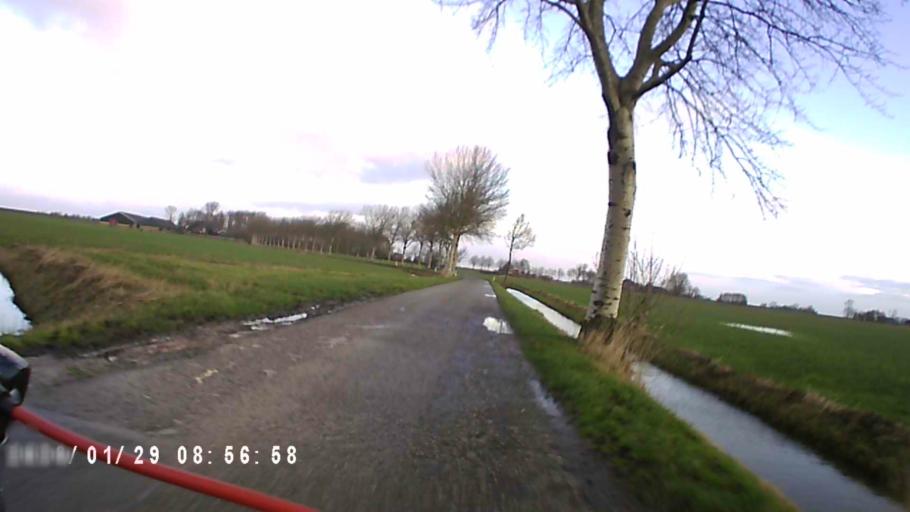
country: NL
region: Groningen
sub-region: Gemeente Zuidhorn
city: Aduard
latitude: 53.3143
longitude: 6.4552
